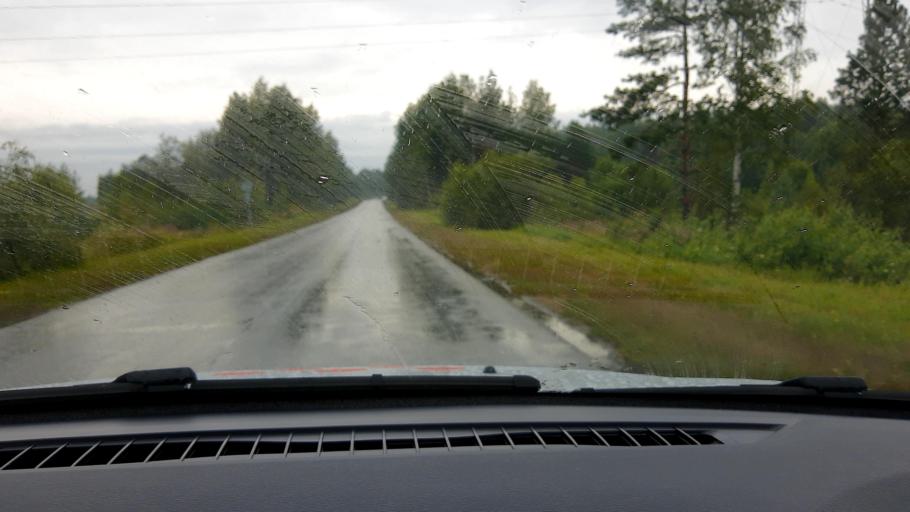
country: RU
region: Nizjnij Novgorod
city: Dal'neye Konstantinovo
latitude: 55.9491
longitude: 43.9730
